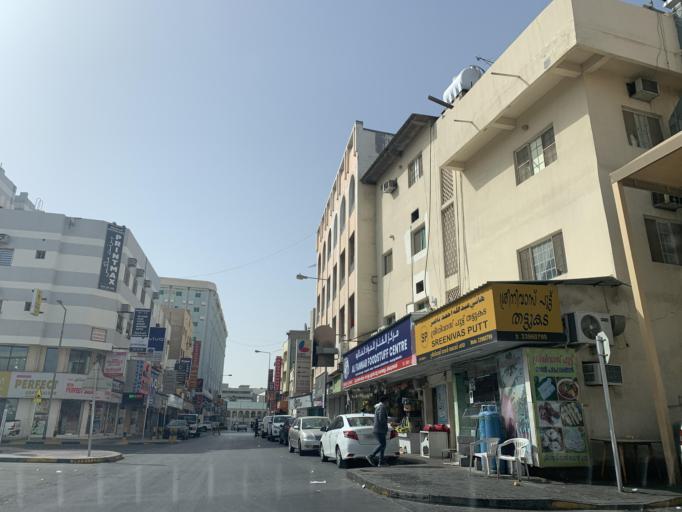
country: BH
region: Manama
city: Manama
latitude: 26.2211
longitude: 50.5712
